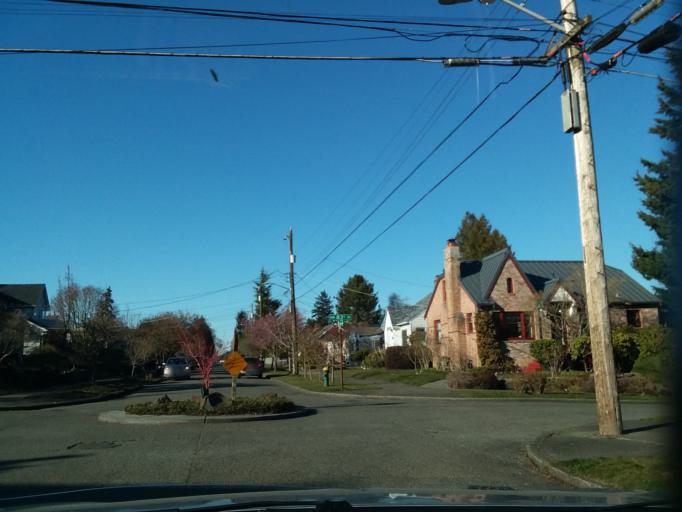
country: US
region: Washington
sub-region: King County
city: Shoreline
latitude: 47.6890
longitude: -122.3673
